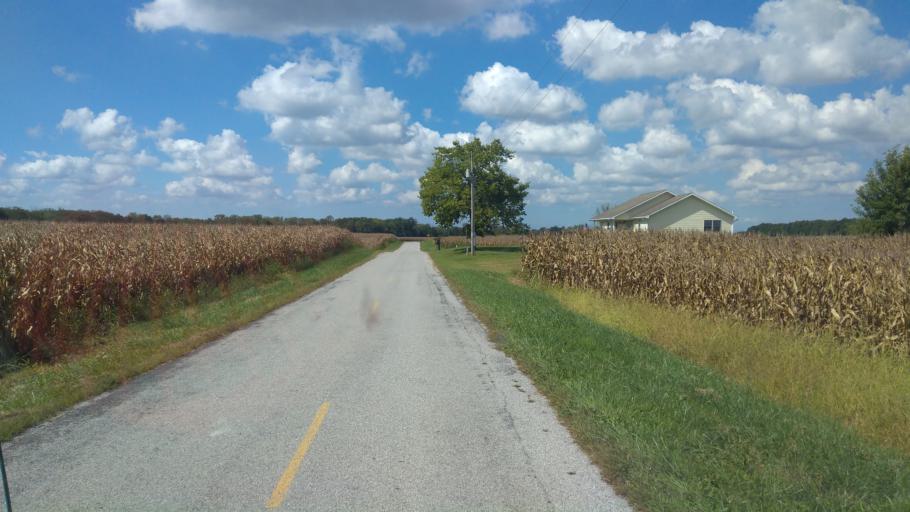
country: US
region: Ohio
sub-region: Wyandot County
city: Upper Sandusky
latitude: 40.6728
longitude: -83.3455
